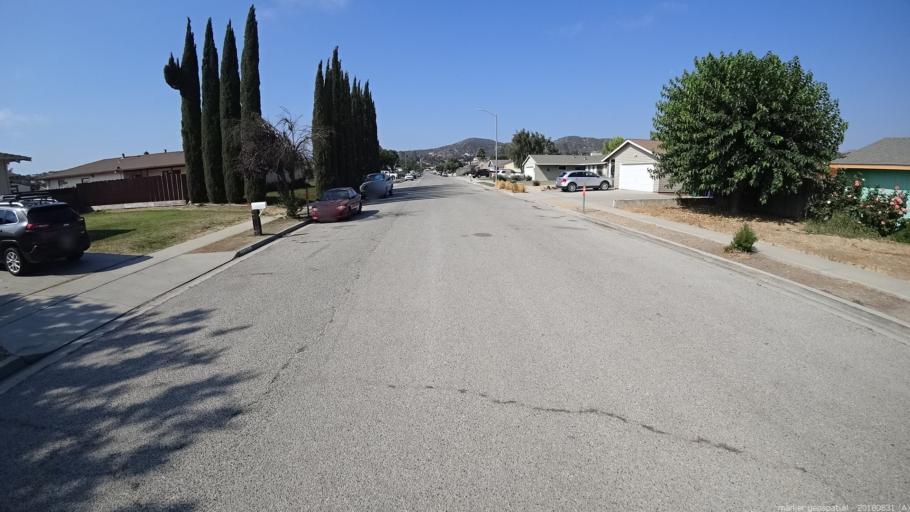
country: US
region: California
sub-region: Monterey County
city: King City
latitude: 36.1863
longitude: -121.1449
